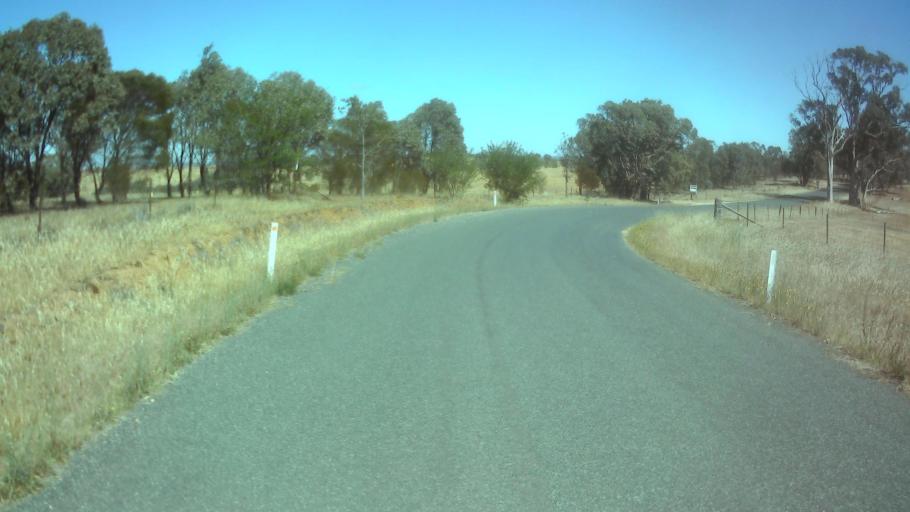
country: AU
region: New South Wales
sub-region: Weddin
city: Grenfell
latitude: -33.9462
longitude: 148.3903
